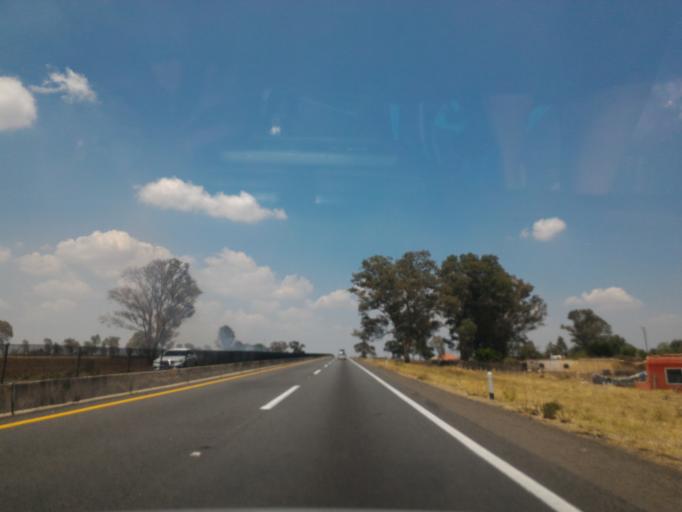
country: MX
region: Jalisco
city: Tepatitlan de Morelos
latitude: 20.8717
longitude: -102.7486
